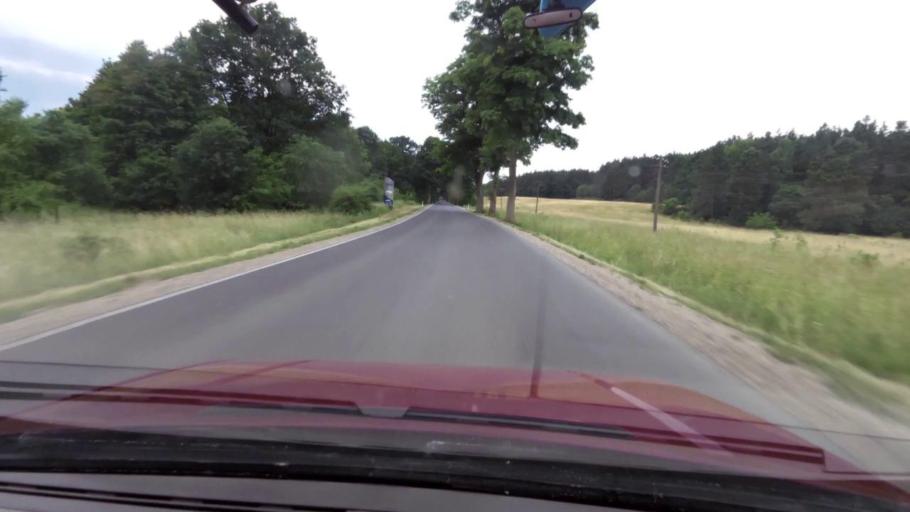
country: PL
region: West Pomeranian Voivodeship
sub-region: Powiat koszalinski
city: Sianow
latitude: 54.1690
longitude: 16.4271
